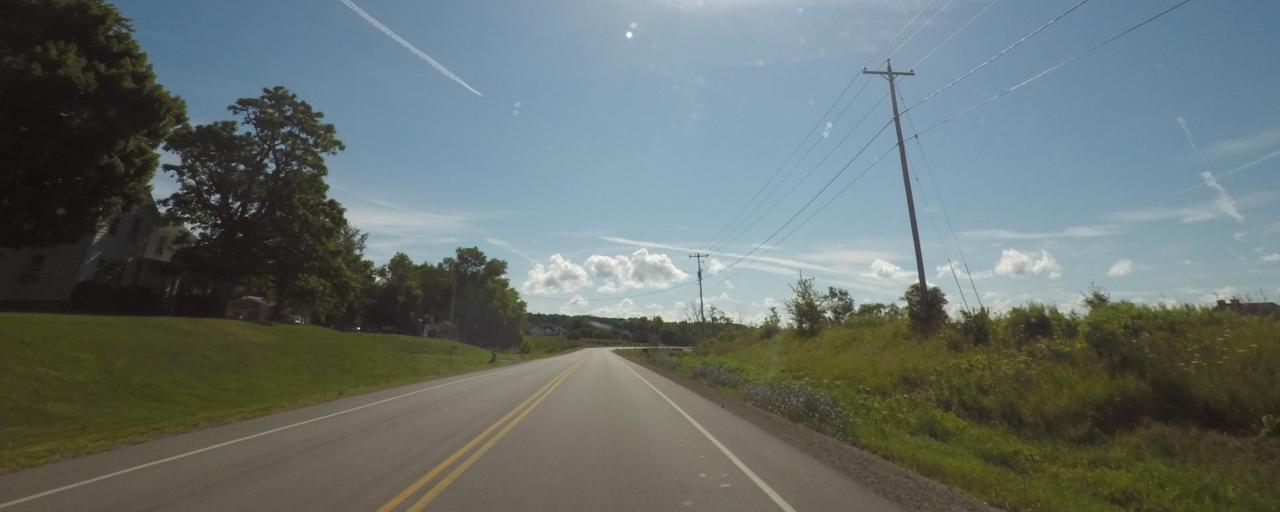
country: US
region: Wisconsin
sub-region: Jefferson County
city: Ixonia
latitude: 43.0761
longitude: -88.6714
